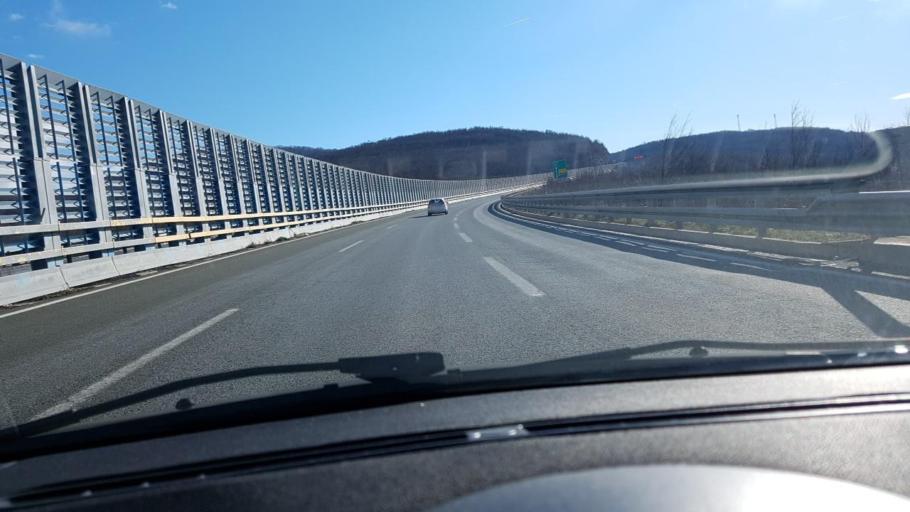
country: HR
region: Primorsko-Goranska
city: Krasica
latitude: 45.3468
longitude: 14.5935
